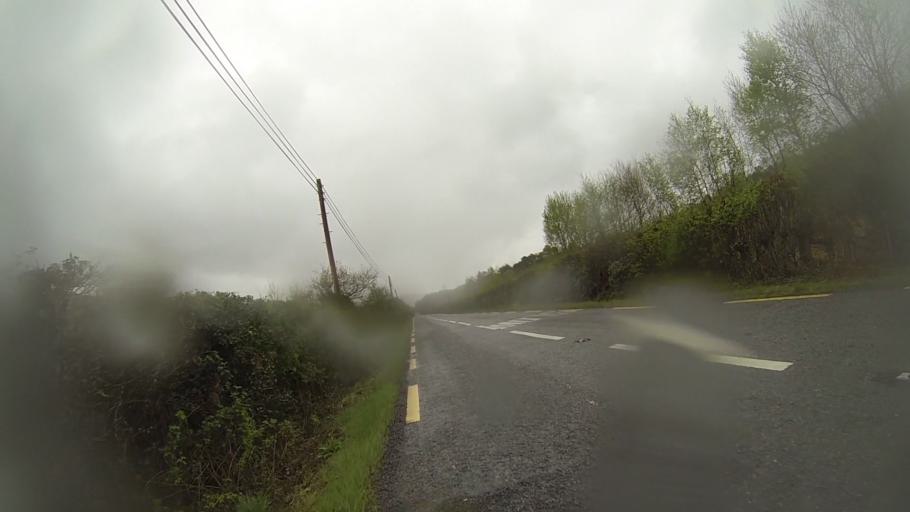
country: IE
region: Munster
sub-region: Ciarrai
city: Kenmare
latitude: 51.8219
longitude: -9.5281
